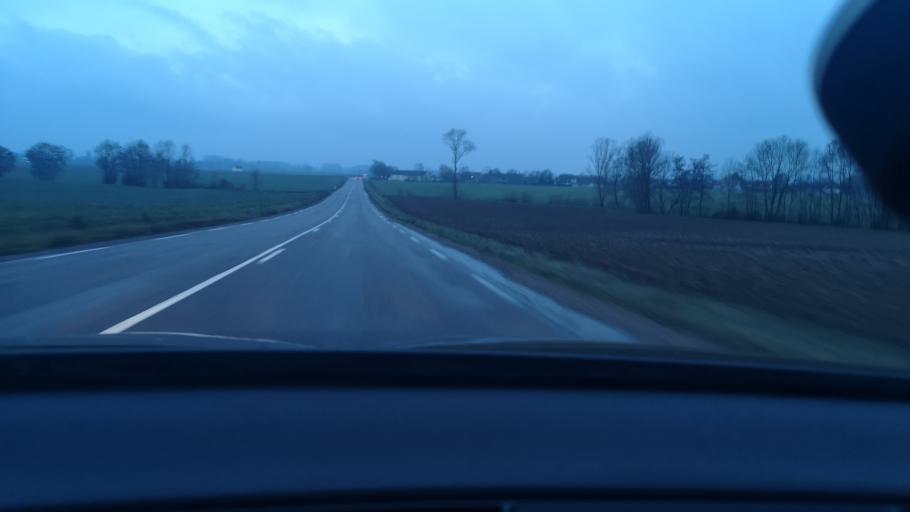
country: FR
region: Bourgogne
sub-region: Departement de la Cote-d'Or
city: Beaune
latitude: 47.0072
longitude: 4.9572
